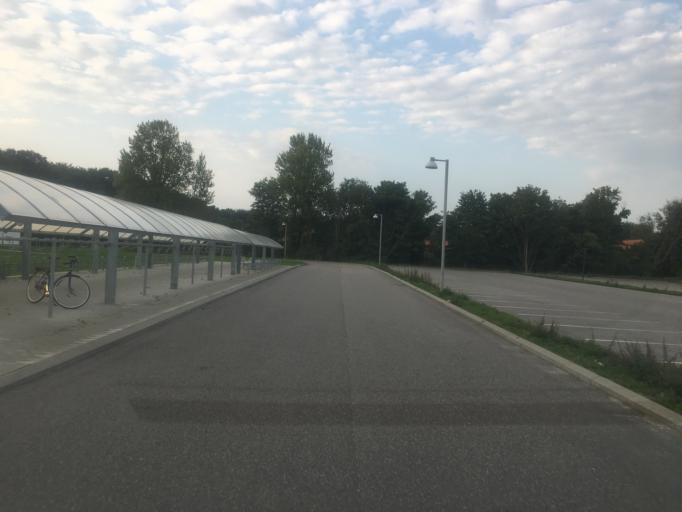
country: DK
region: South Denmark
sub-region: Tonder Kommune
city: Tonder
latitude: 54.9408
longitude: 8.8583
